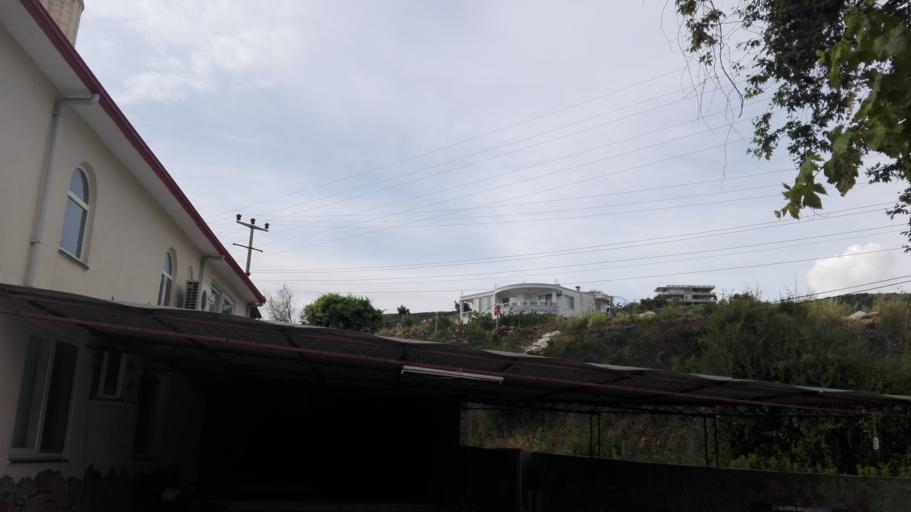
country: TR
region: Antalya
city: Demirtas
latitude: 36.4320
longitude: 32.1627
